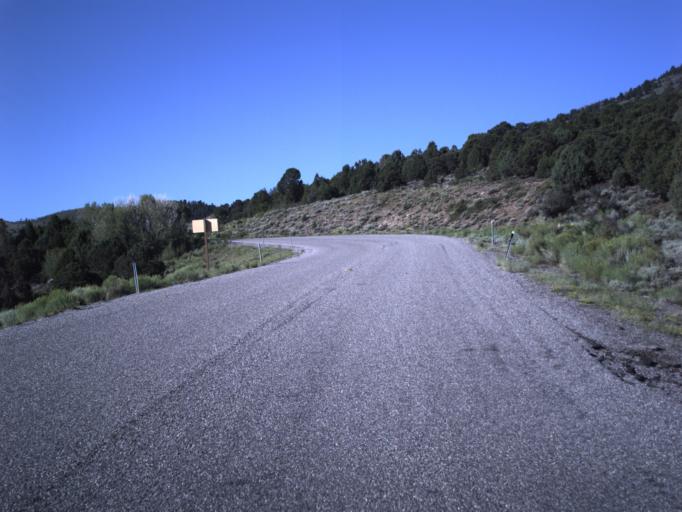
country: US
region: Utah
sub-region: Wayne County
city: Loa
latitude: 38.6138
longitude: -111.4593
